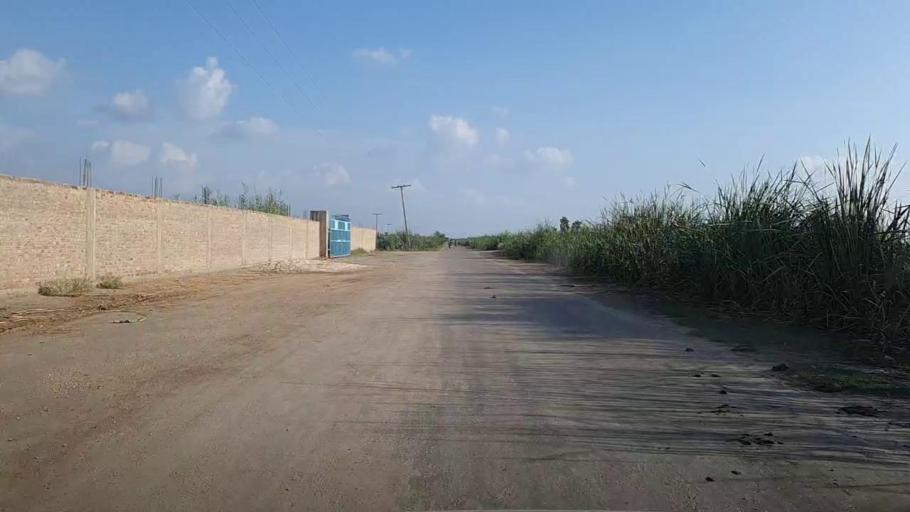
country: PK
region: Sindh
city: Hingorja
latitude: 27.0967
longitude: 68.4024
